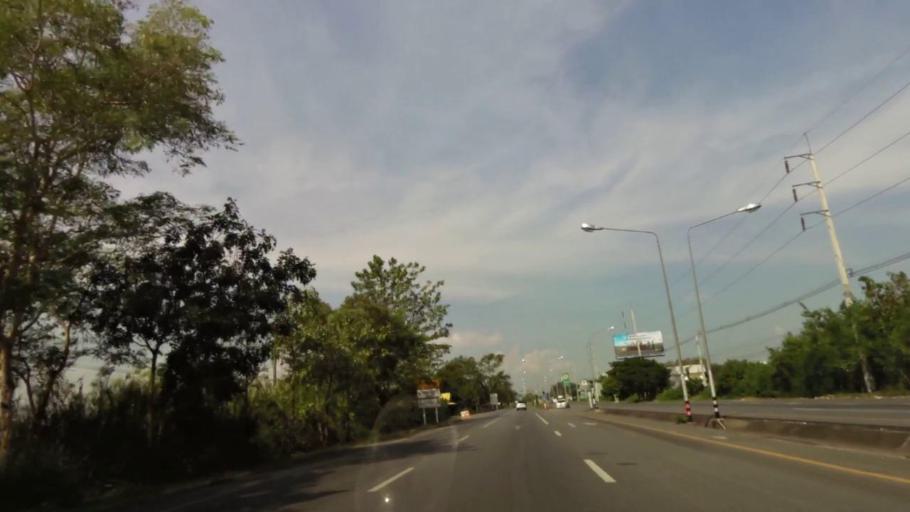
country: TH
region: Uttaradit
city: Uttaradit
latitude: 17.5824
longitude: 100.1414
